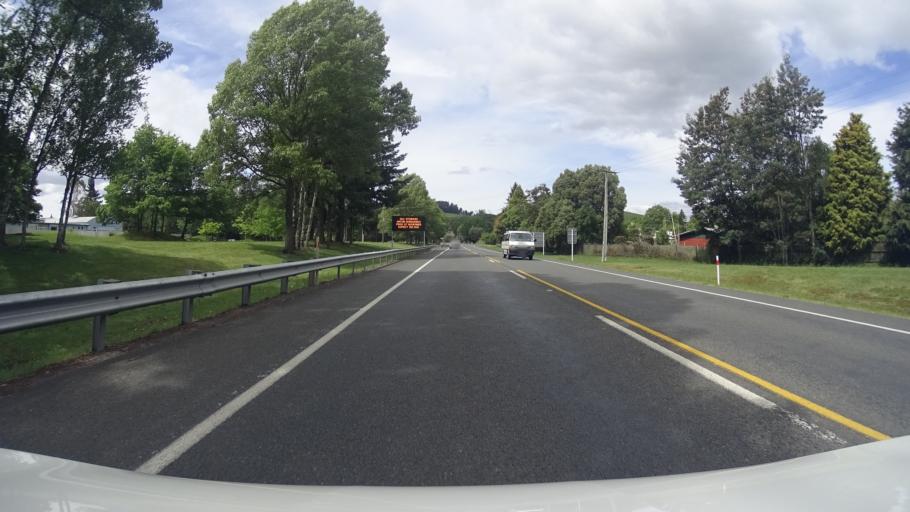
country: NZ
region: Waikato
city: Turangi
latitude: -38.9894
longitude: 175.8132
